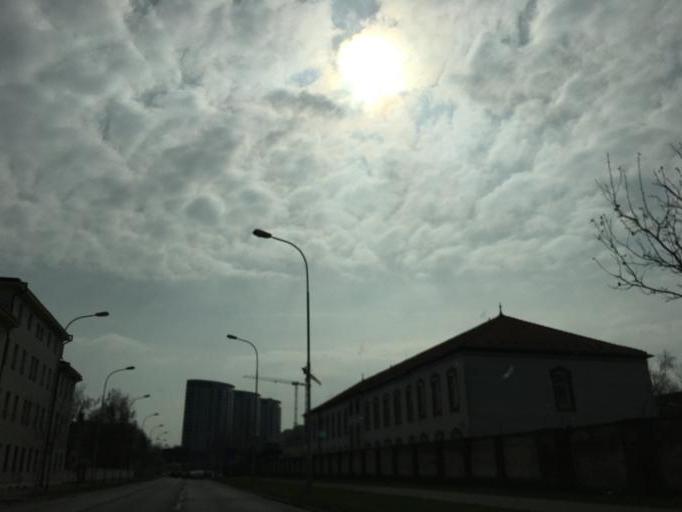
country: SK
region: Bratislavsky
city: Bratislava
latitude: 48.1668
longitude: 17.1331
